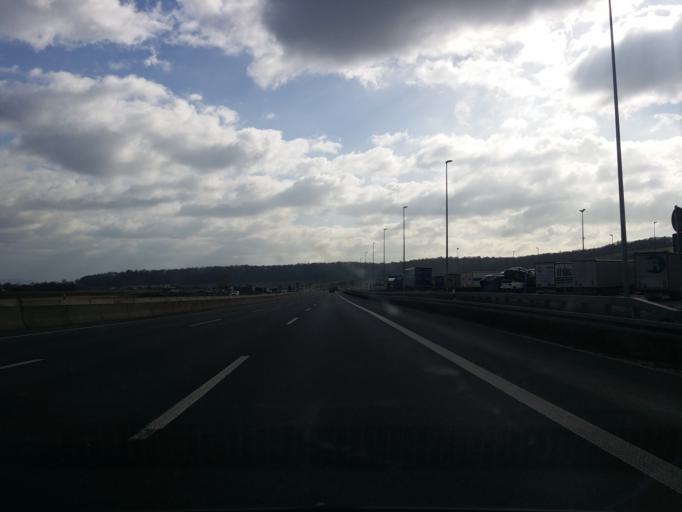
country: DE
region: Lower Saxony
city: Bovenden
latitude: 51.6069
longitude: 9.9067
